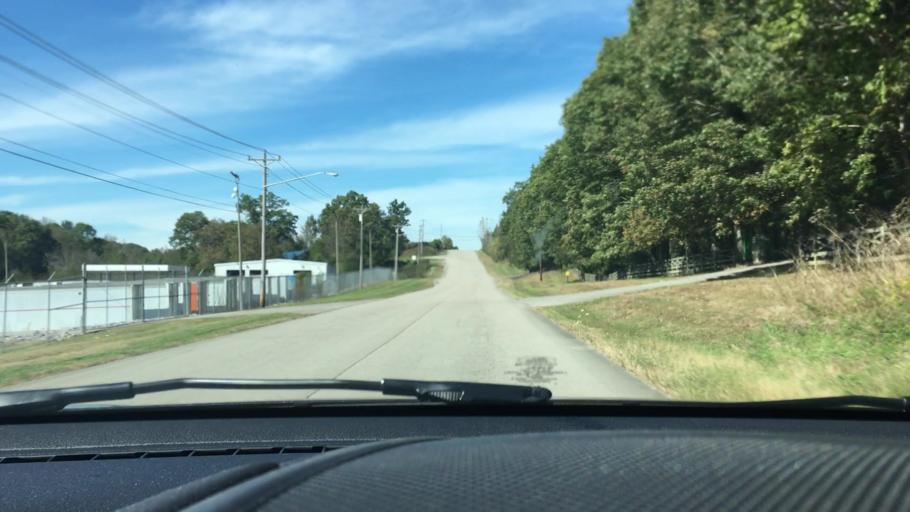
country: US
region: Tennessee
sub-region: Giles County
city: Pulaski
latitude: 35.2205
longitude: -87.0646
